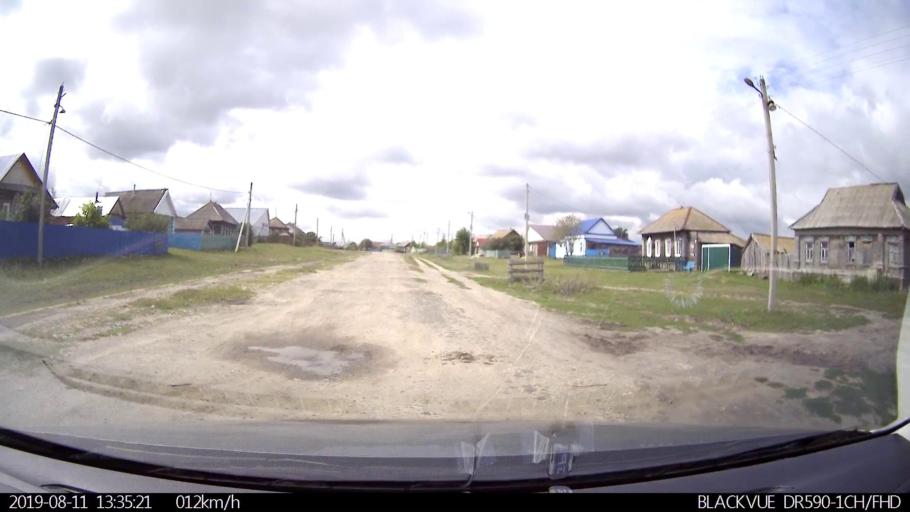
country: RU
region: Ulyanovsk
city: Ignatovka
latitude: 53.8598
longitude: 47.5906
